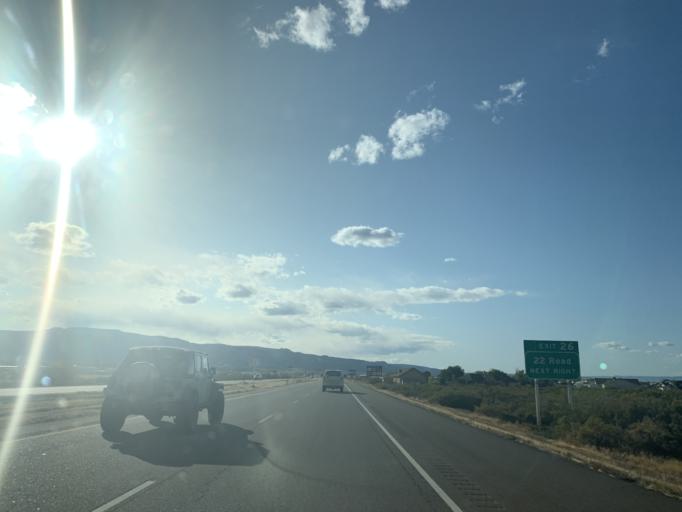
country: US
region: Colorado
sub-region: Mesa County
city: Redlands
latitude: 39.1141
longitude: -108.6296
